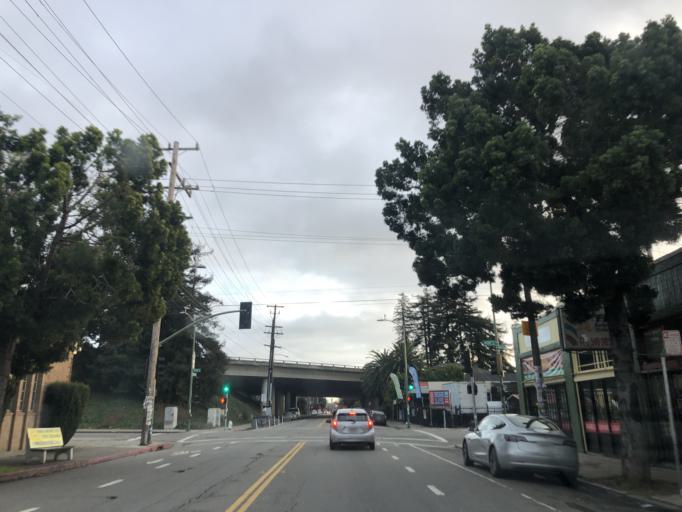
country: US
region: California
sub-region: Alameda County
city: Emeryville
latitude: 37.8409
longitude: -122.2646
